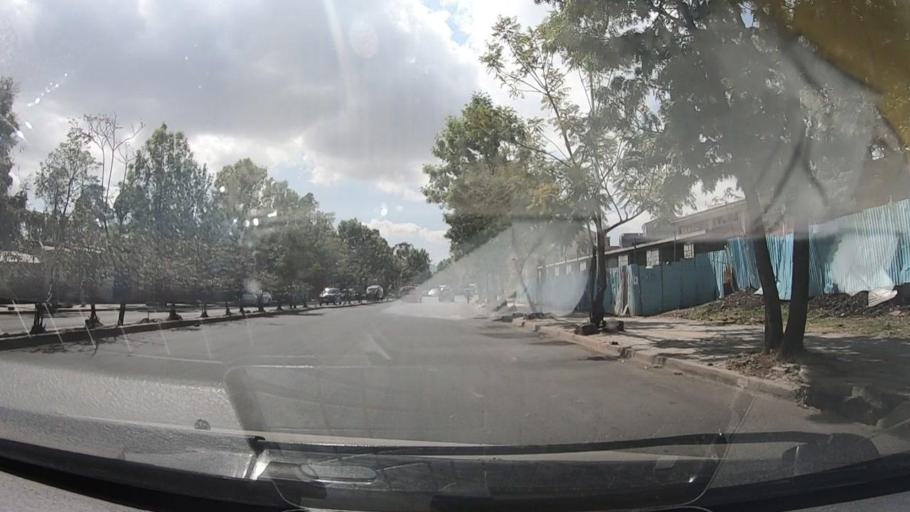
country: ET
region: Adis Abeba
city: Addis Ababa
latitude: 8.9714
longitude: 38.7243
